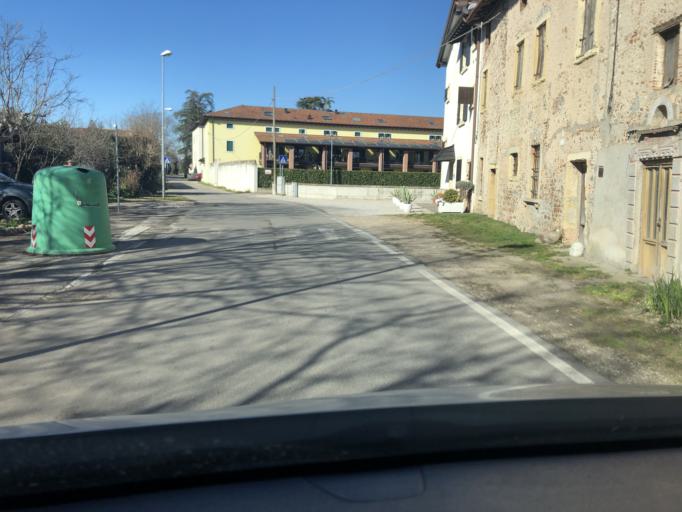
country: IT
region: Veneto
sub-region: Provincia di Verona
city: Bassone
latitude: 45.4552
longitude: 10.8761
